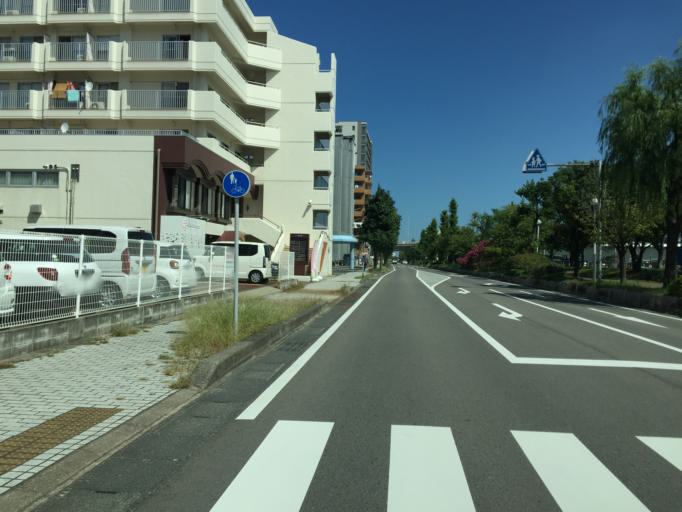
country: JP
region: Niigata
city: Niigata-shi
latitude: 37.9220
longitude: 139.0532
